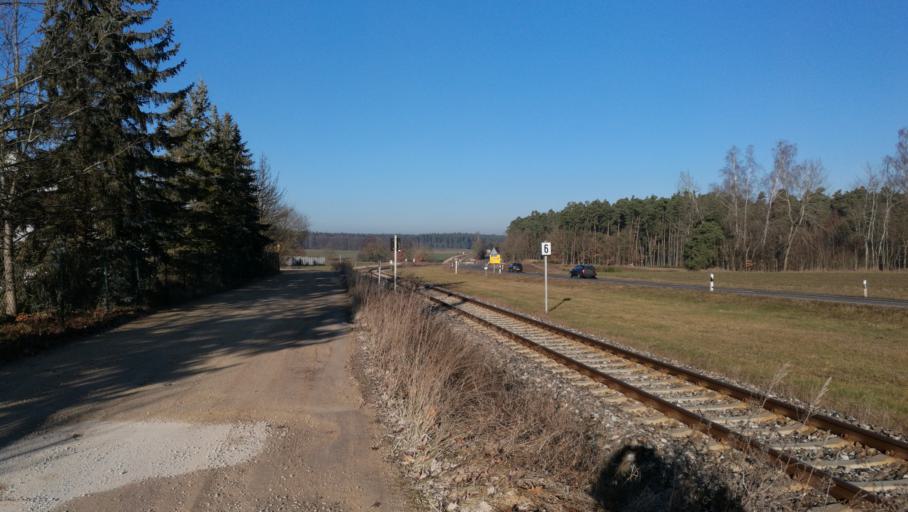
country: DE
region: Bavaria
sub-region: Regierungsbezirk Mittelfranken
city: Roth
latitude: 49.2163
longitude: 11.1346
